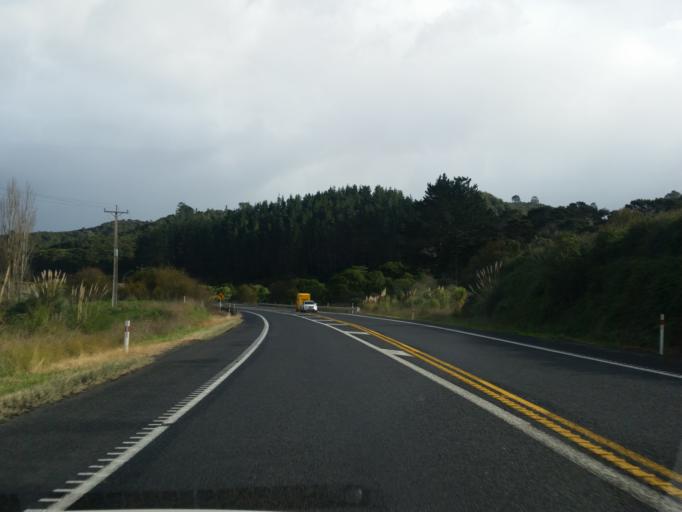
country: NZ
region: Auckland
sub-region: Auckland
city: Pukekohe East
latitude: -37.2121
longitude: 175.0817
